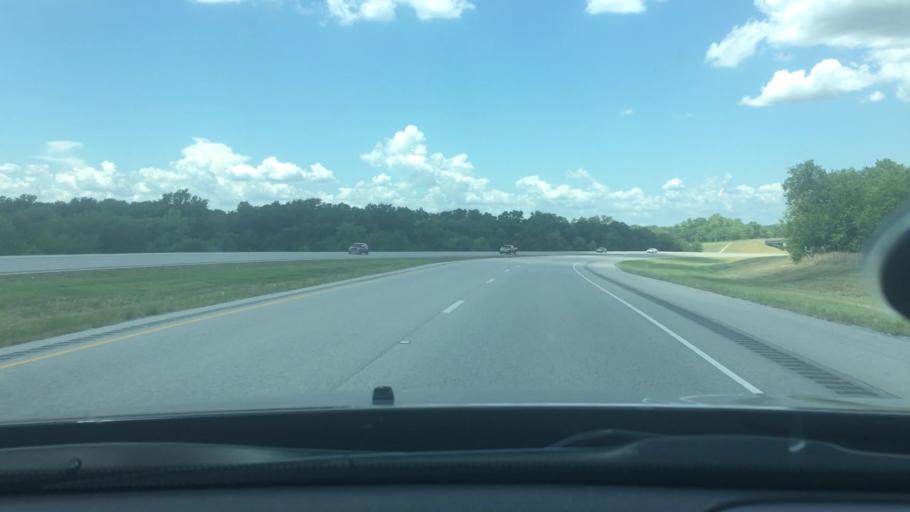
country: US
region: Oklahoma
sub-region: Bryan County
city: Calera
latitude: 33.9791
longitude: -96.4264
